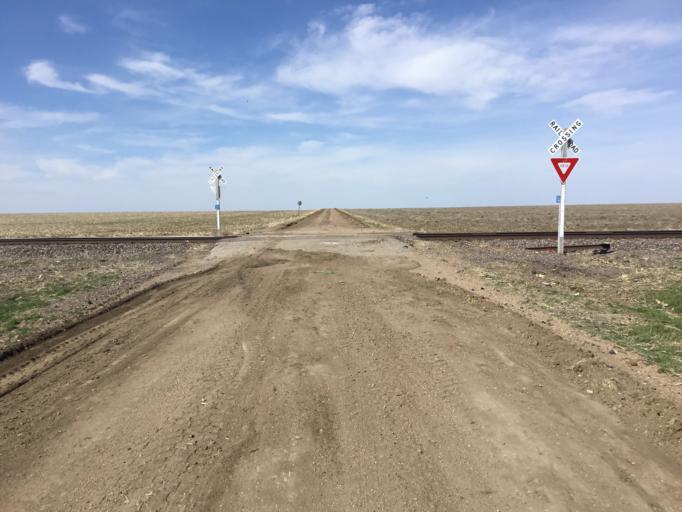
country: US
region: Kansas
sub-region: Trego County
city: WaKeeney
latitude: 39.0382
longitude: -100.0743
